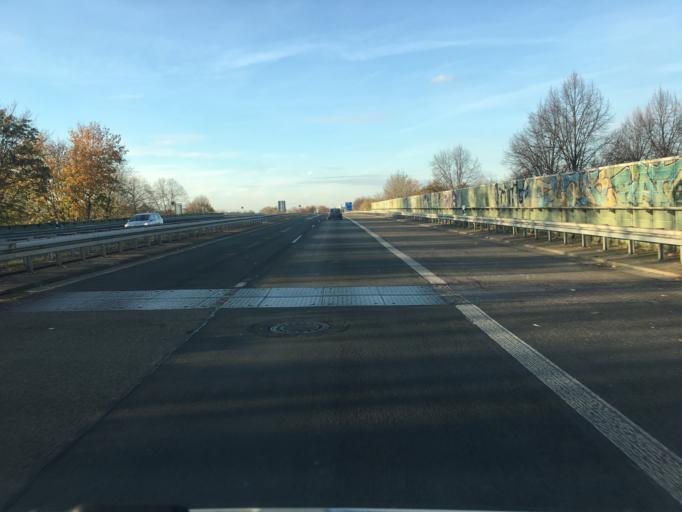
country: DE
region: North Rhine-Westphalia
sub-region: Regierungsbezirk Koln
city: Merheim
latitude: 50.9441
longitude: 7.0611
